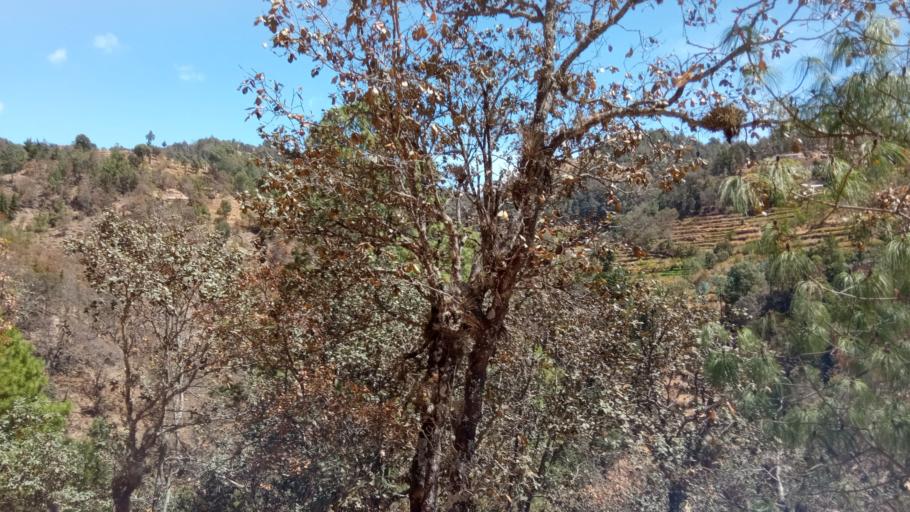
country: GT
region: San Marcos
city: Tejutla
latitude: 15.1362
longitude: -91.7925
